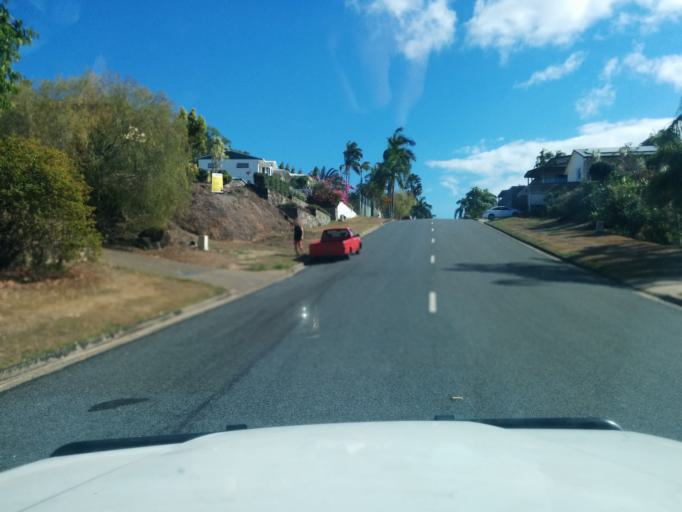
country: AU
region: Queensland
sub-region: Cairns
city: Woree
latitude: -16.9511
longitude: 145.7332
